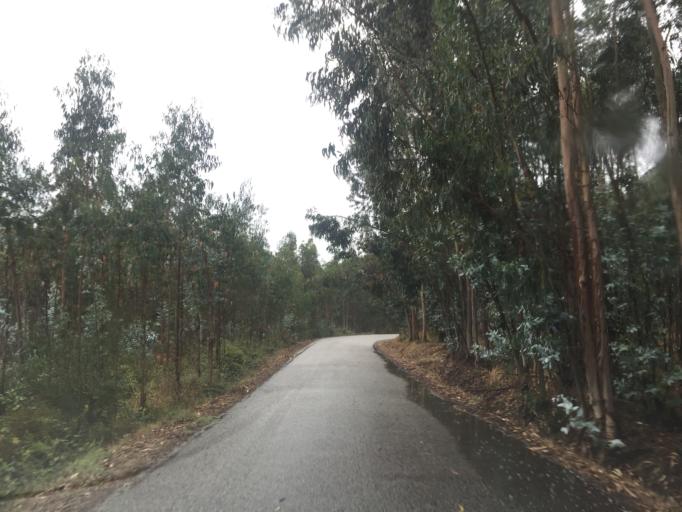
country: PT
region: Leiria
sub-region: Pombal
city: Lourical
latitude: 40.0503
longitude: -8.7809
